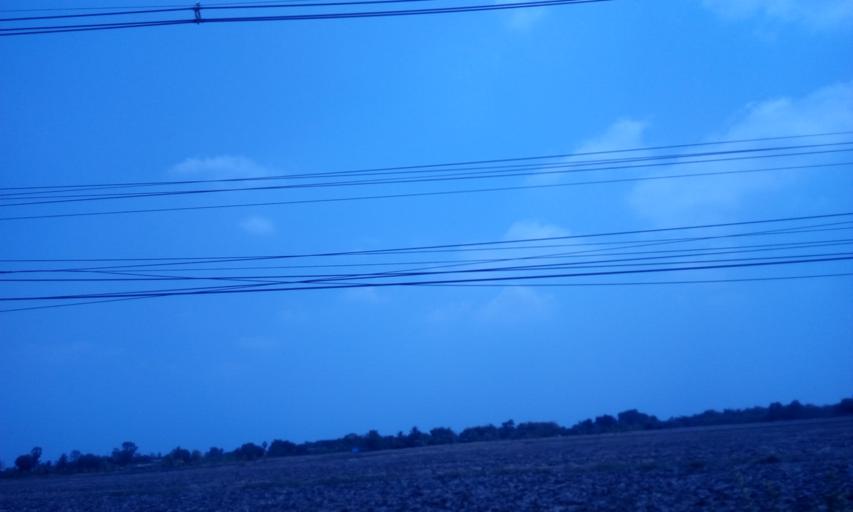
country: TH
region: Chachoengsao
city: Chachoengsao
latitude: 13.7360
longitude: 101.0860
